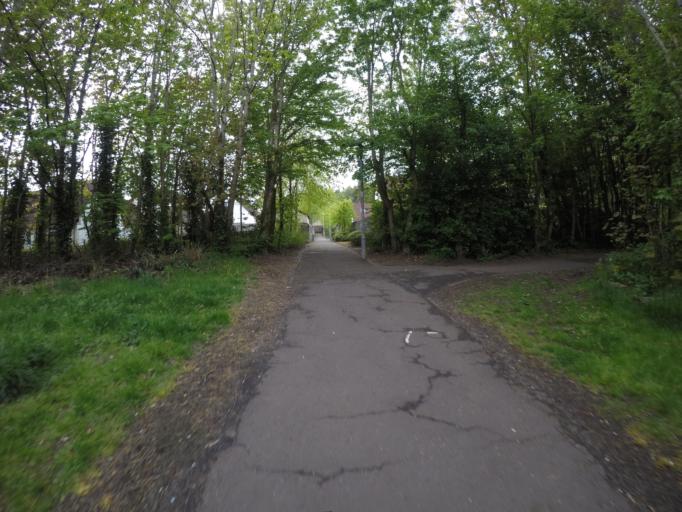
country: GB
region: Scotland
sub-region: North Ayrshire
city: Irvine
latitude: 55.6331
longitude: -4.6411
